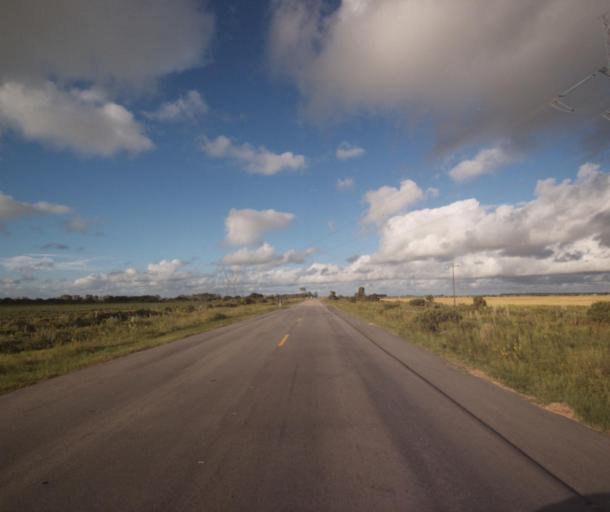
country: BR
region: Rio Grande do Sul
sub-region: Rio Grande
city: Rio Grande
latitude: -32.2125
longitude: -52.4568
